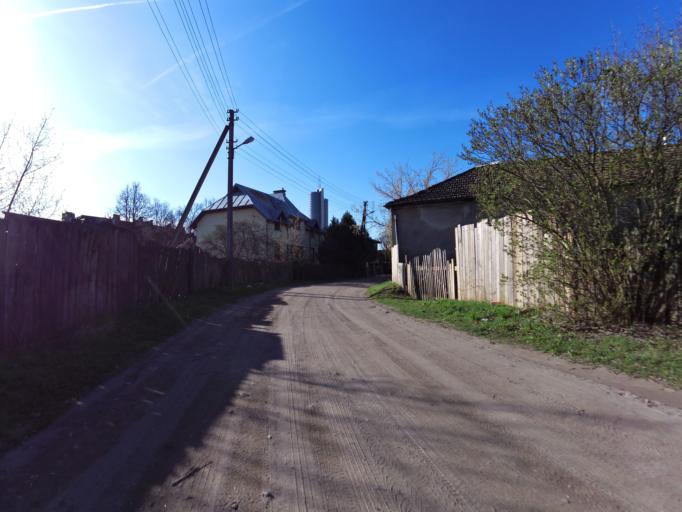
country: LT
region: Vilnius County
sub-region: Vilnius
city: Vilnius
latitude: 54.7009
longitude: 25.2756
